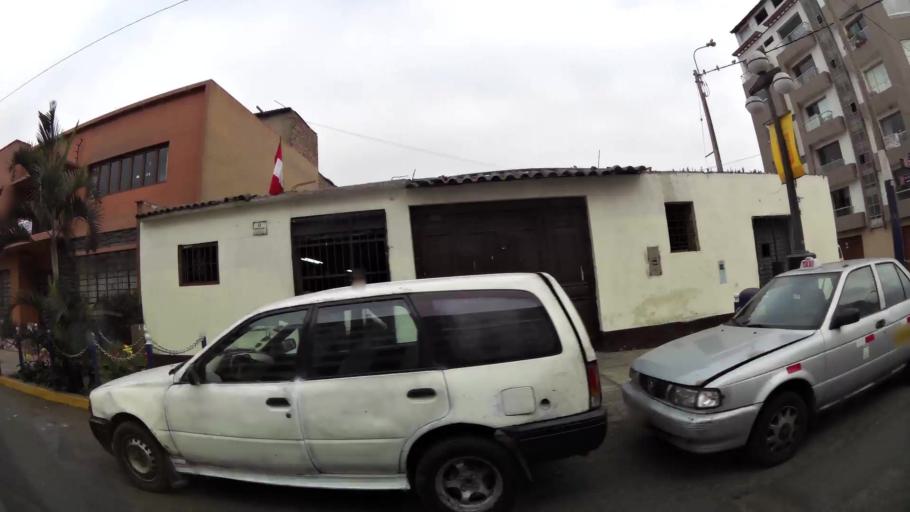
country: PE
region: Lima
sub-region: Lima
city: Surco
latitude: -12.1657
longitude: -77.0231
